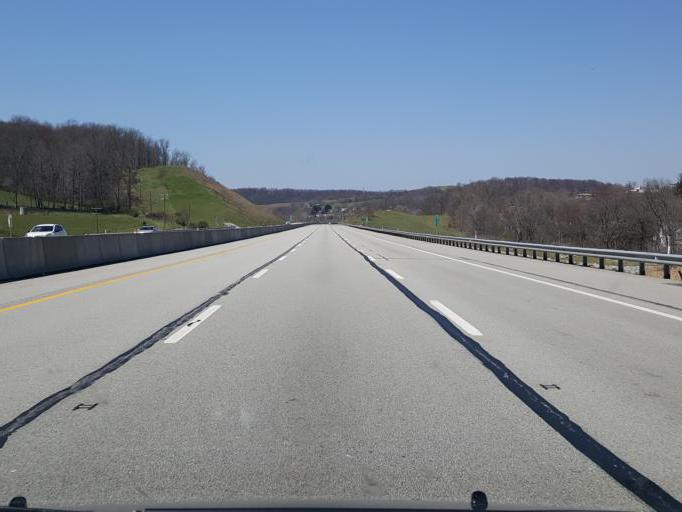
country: US
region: Pennsylvania
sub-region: Westmoreland County
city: New Stanton
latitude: 40.2635
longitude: -79.6549
